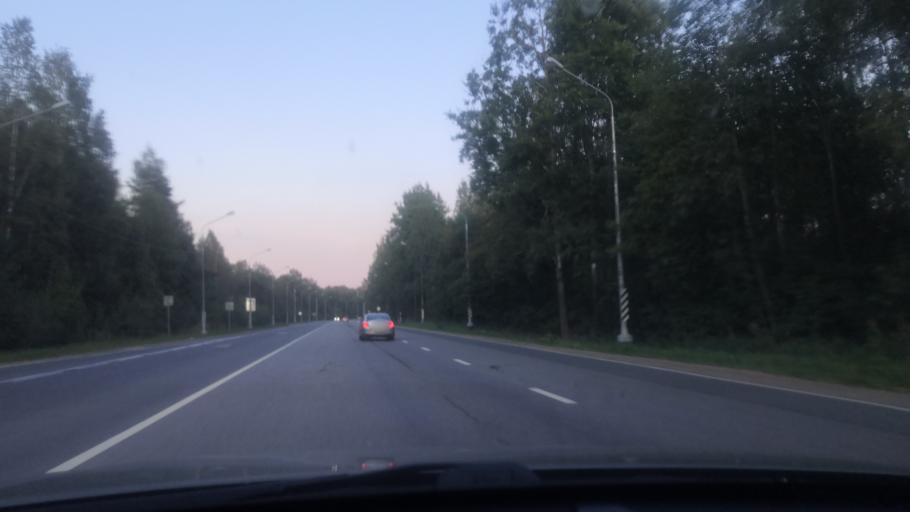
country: RU
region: St.-Petersburg
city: Beloostrov
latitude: 60.1958
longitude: 30.0586
